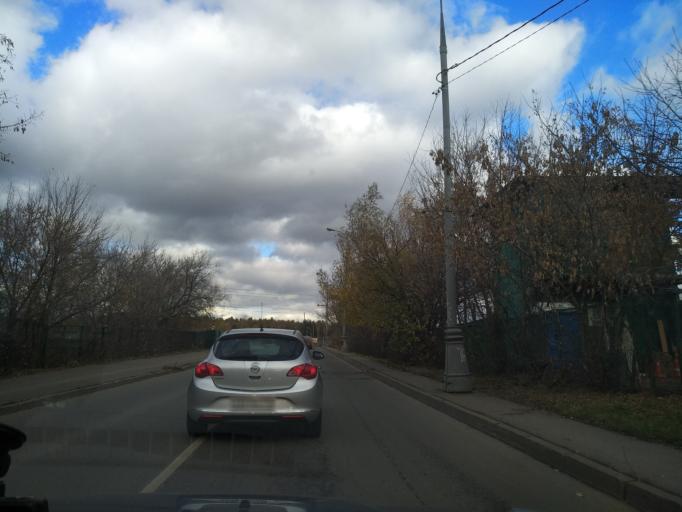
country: RU
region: Moscow
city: Bibirevo
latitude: 55.9015
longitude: 37.6142
